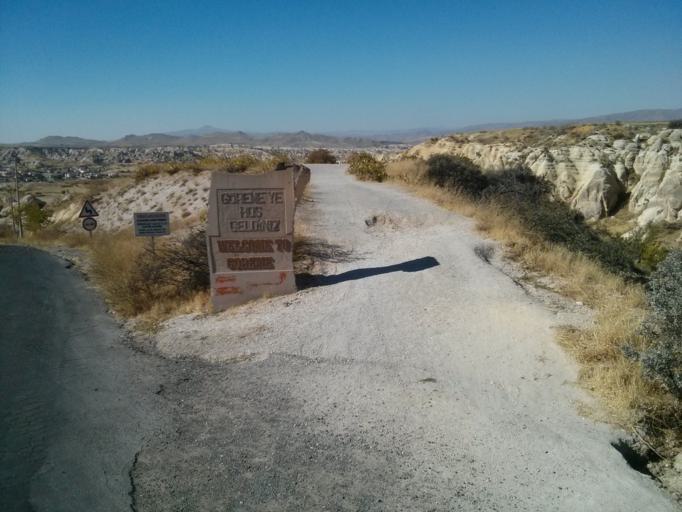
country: TR
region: Nevsehir
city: Goereme
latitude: 38.6398
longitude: 34.8480
